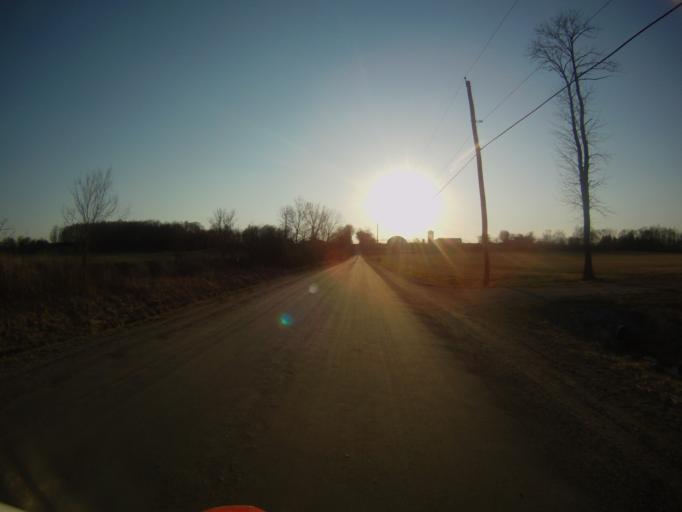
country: US
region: Vermont
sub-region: Addison County
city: Middlebury (village)
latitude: 44.0420
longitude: -73.1115
